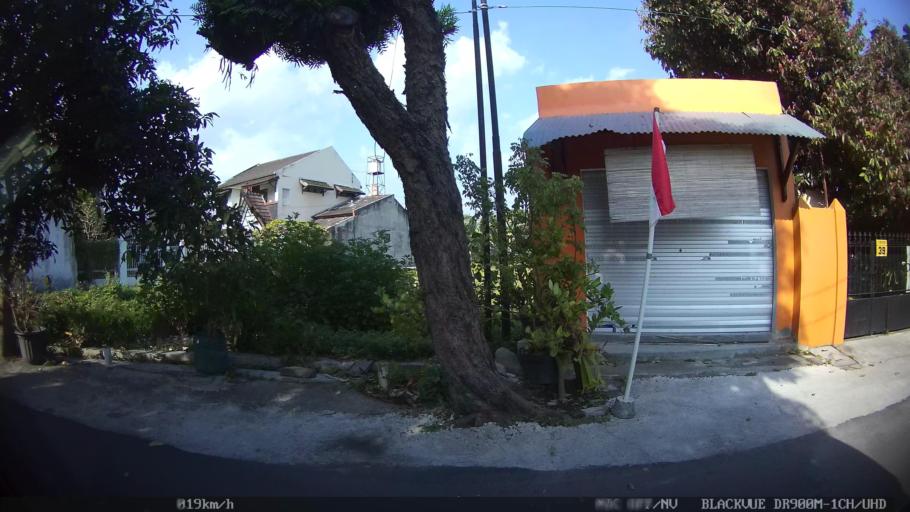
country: ID
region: Daerah Istimewa Yogyakarta
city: Yogyakarta
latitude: -7.8211
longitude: 110.3809
